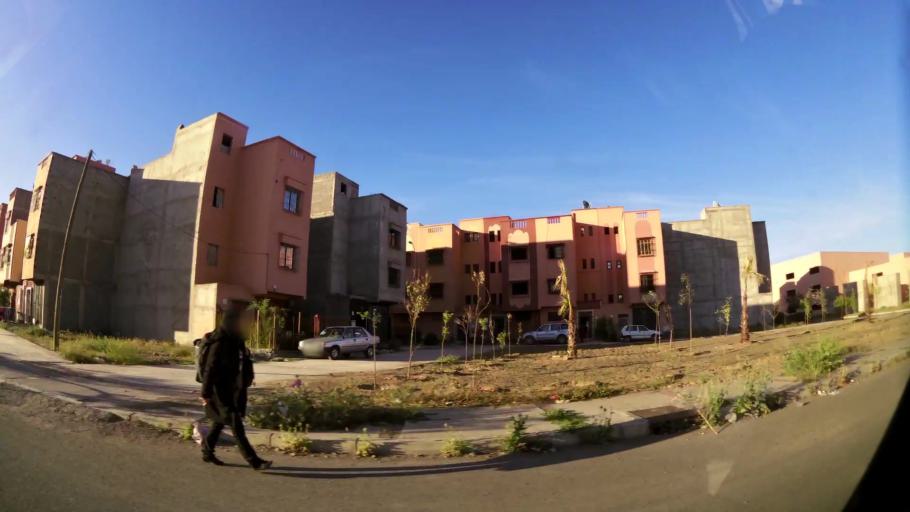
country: MA
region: Marrakech-Tensift-Al Haouz
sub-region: Marrakech
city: Marrakesh
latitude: 31.7453
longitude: -8.1158
